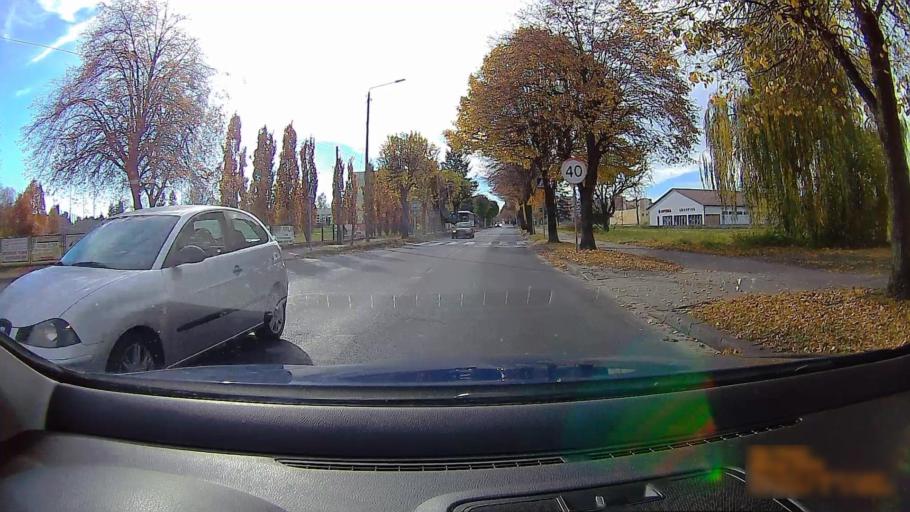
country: PL
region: Greater Poland Voivodeship
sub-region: Powiat ostrzeszowski
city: Ostrzeszow
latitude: 51.4250
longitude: 17.9385
